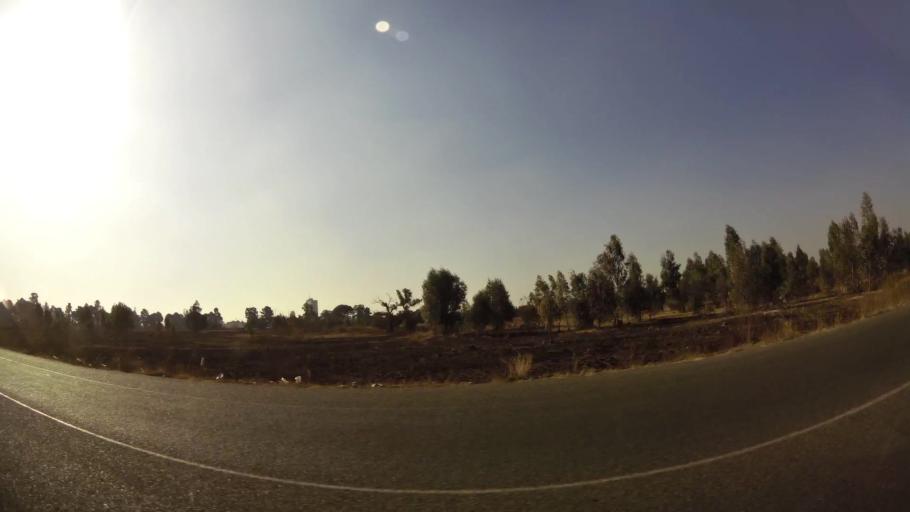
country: ZA
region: Gauteng
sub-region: West Rand District Municipality
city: Randfontein
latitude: -26.1777
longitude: 27.7137
